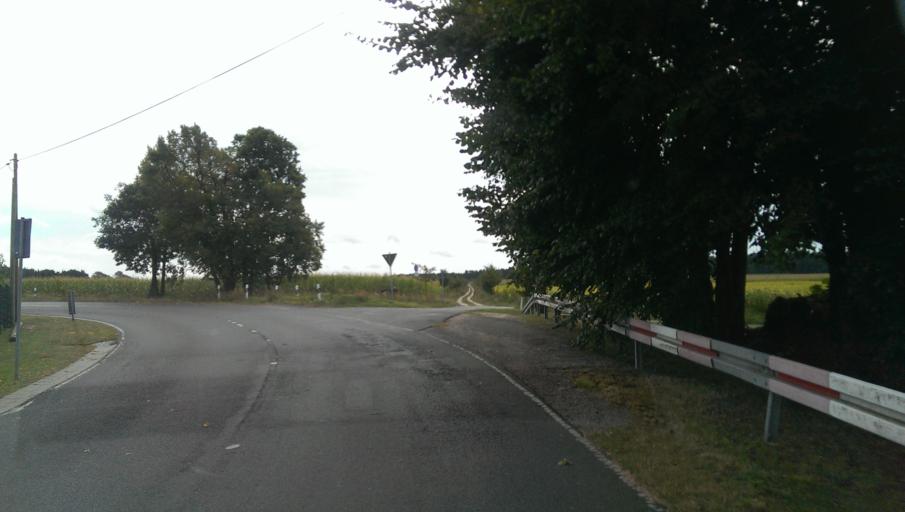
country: DE
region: Brandenburg
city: Trebbin
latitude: 52.1984
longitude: 13.2102
